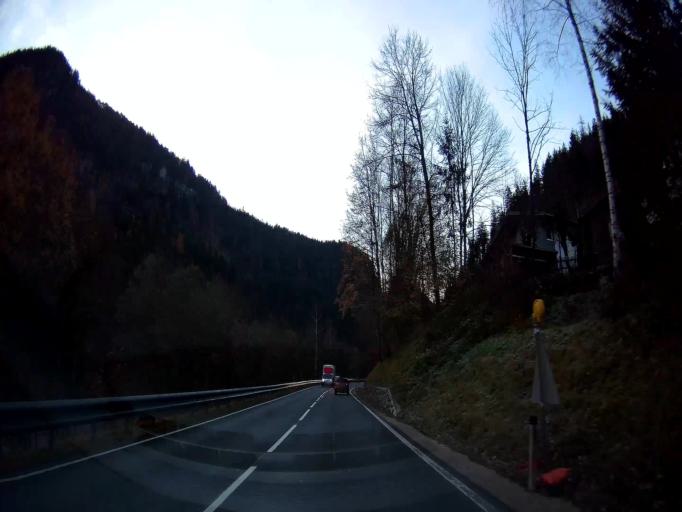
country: AT
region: Salzburg
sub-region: Politischer Bezirk Zell am See
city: Unken
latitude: 47.6440
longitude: 12.7248
